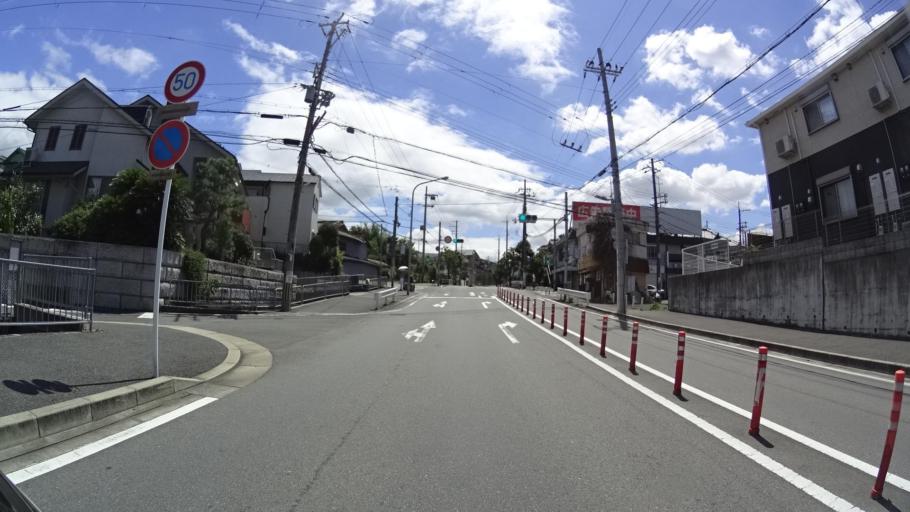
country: JP
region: Kyoto
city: Yawata
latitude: 34.8779
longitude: 135.6836
